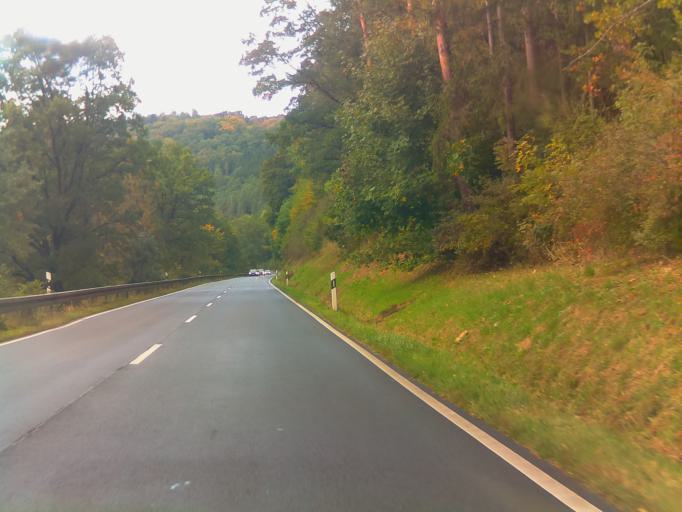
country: DE
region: Baden-Wuerttemberg
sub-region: Karlsruhe Region
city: Hardheim
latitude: 49.6127
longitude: 9.4623
